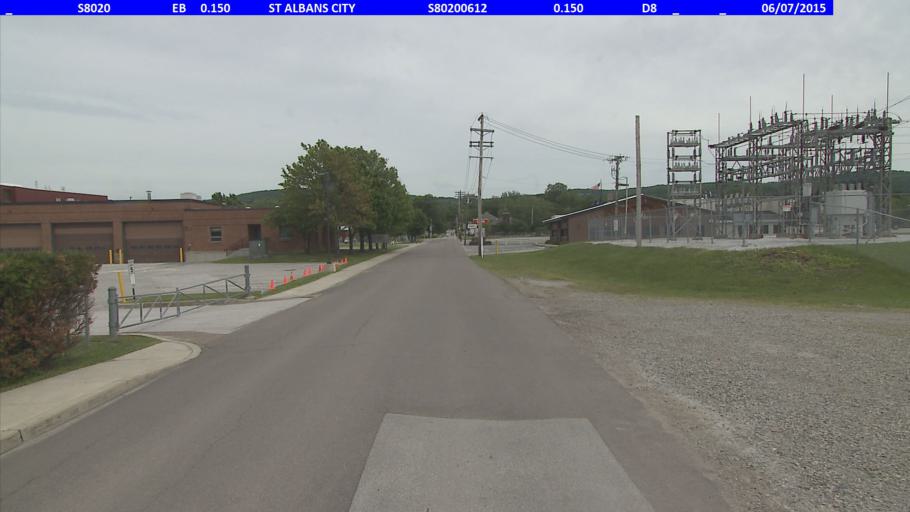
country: US
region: Vermont
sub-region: Franklin County
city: Saint Albans
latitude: 44.8082
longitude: -73.0909
